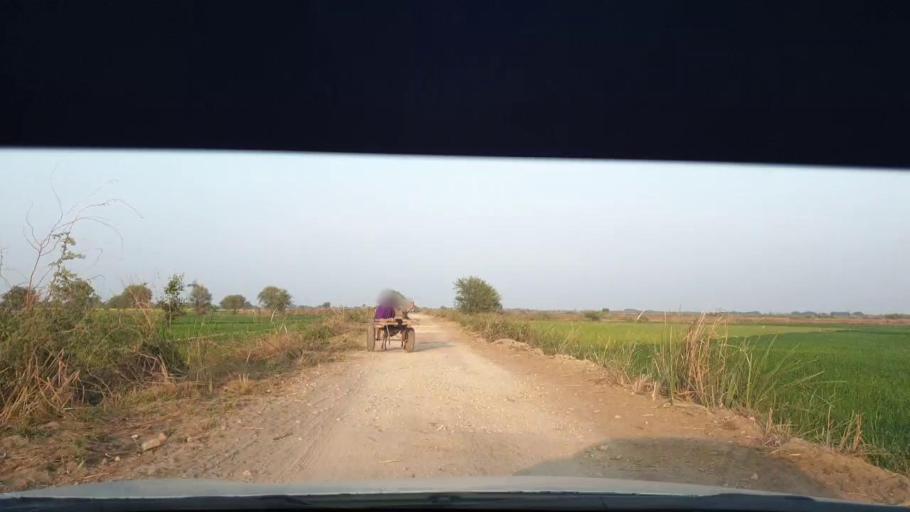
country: PK
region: Sindh
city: Berani
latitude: 25.7434
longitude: 68.9706
